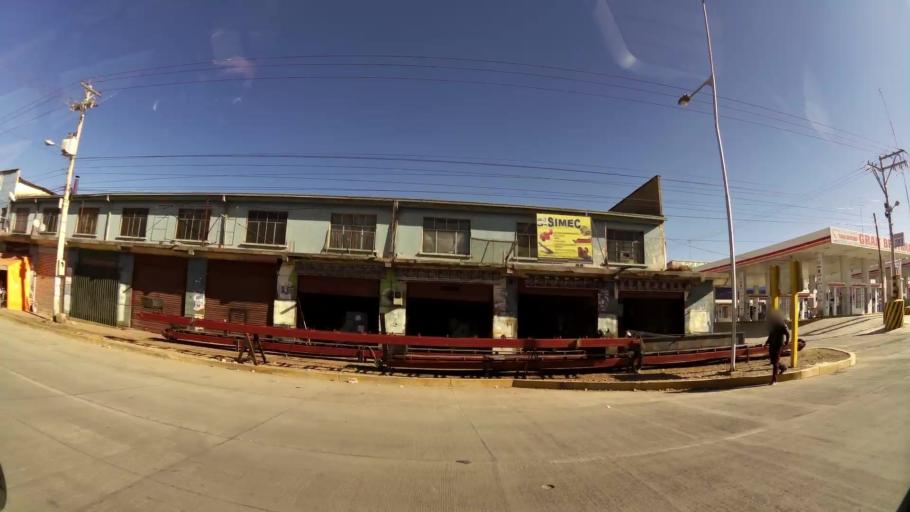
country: BO
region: La Paz
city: La Paz
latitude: -16.5232
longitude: -68.1805
